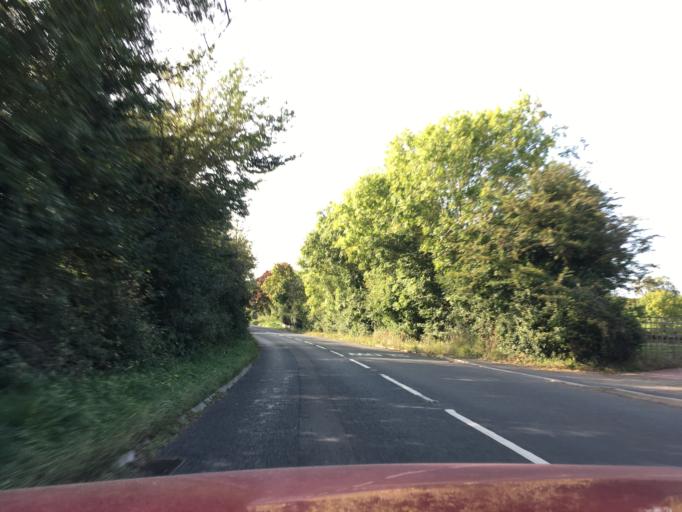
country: GB
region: England
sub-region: Gloucestershire
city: Tewkesbury
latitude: 51.9579
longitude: -2.2446
